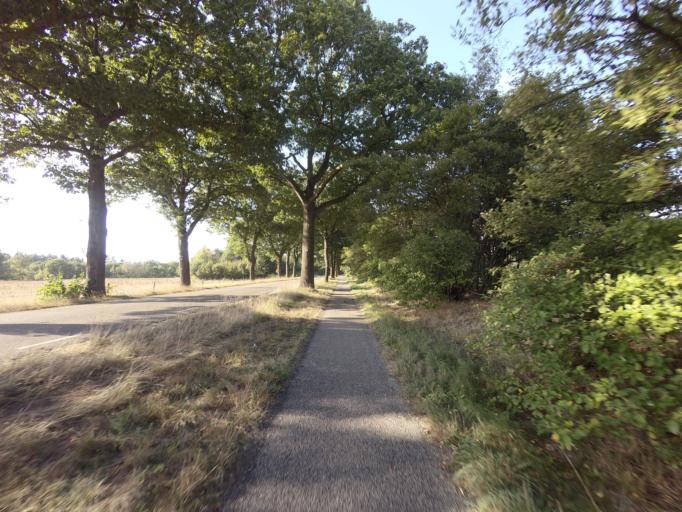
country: NL
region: North Brabant
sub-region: Gemeente Heeze-Leende
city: Heeze
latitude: 51.3753
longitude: 5.6252
